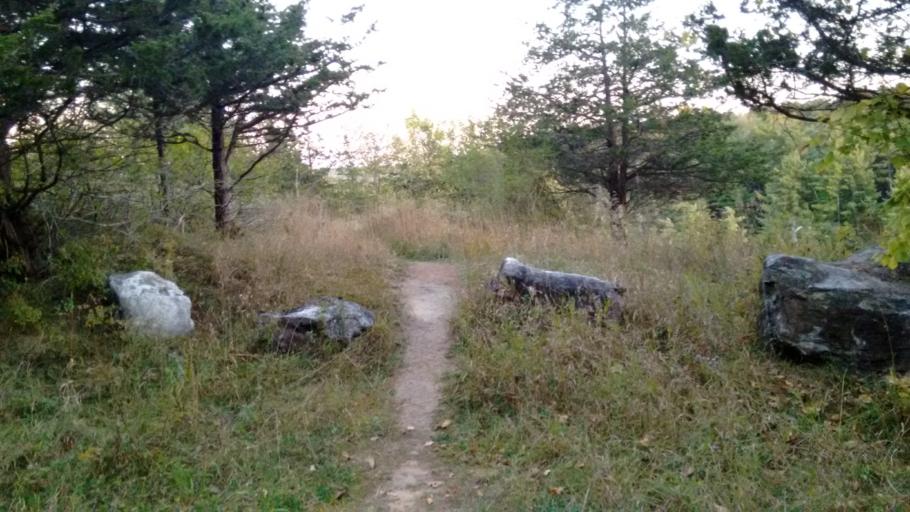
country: CA
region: Ontario
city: Kingston
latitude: 44.5063
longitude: -76.4046
